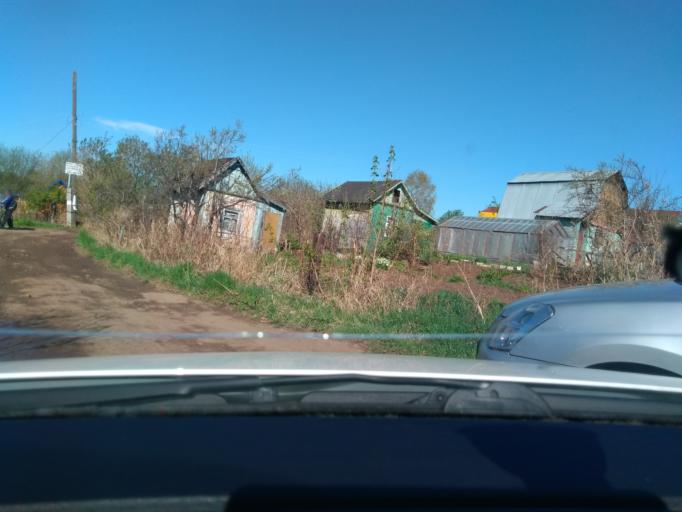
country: RU
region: Perm
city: Lobanovo
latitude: 57.8680
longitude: 56.3045
